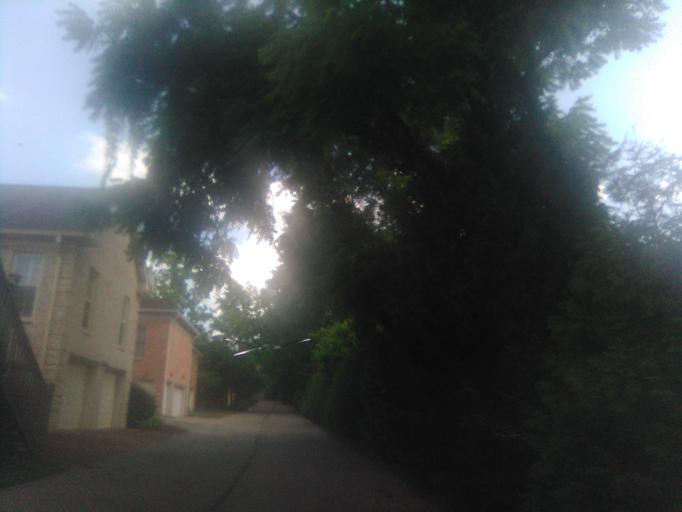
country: US
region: Tennessee
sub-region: Davidson County
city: Belle Meade
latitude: 36.1051
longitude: -86.8297
